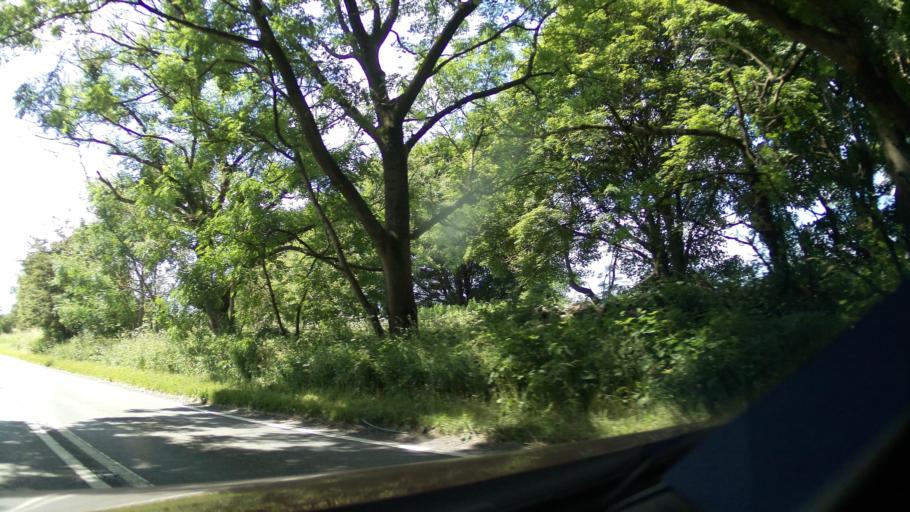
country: GB
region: England
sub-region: Derbyshire
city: Ashbourne
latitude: 53.1053
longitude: -1.7648
